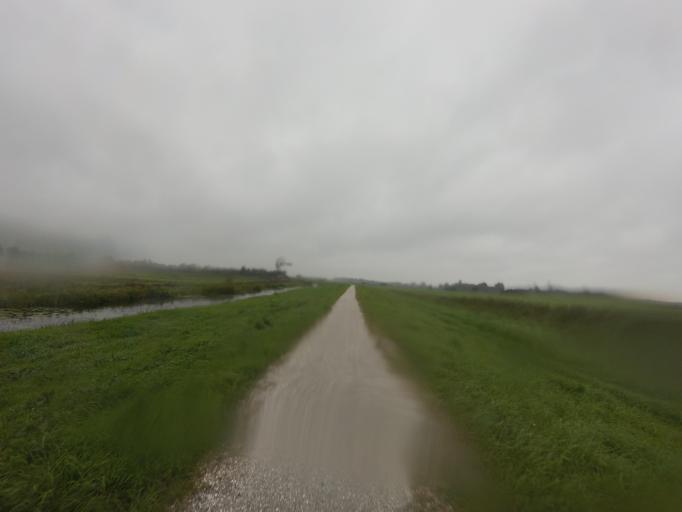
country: NL
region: Friesland
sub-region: Gemeente Smallingerland
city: Oudega
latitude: 53.1027
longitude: 5.9743
